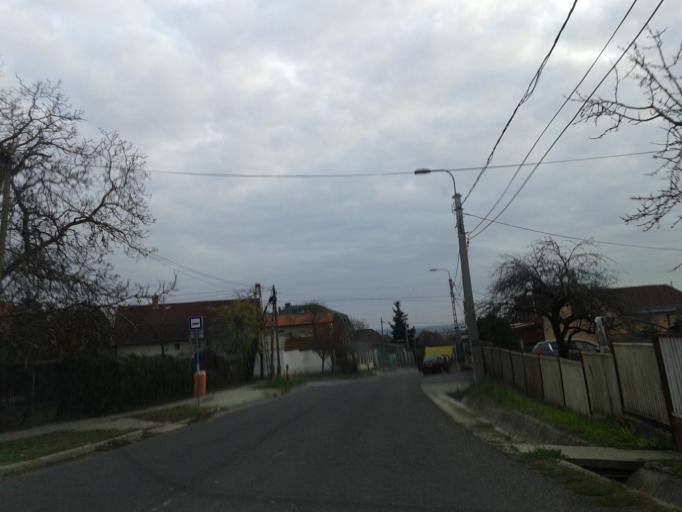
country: HU
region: Pest
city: Diosd
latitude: 47.4070
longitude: 18.9914
